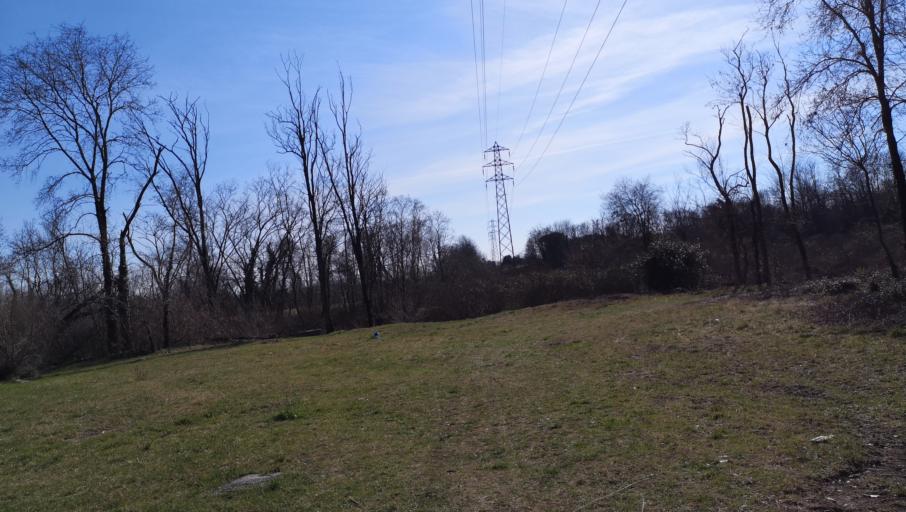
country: IT
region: Friuli Venezia Giulia
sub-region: Provincia di Udine
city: Passons
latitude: 46.0698
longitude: 13.2017
